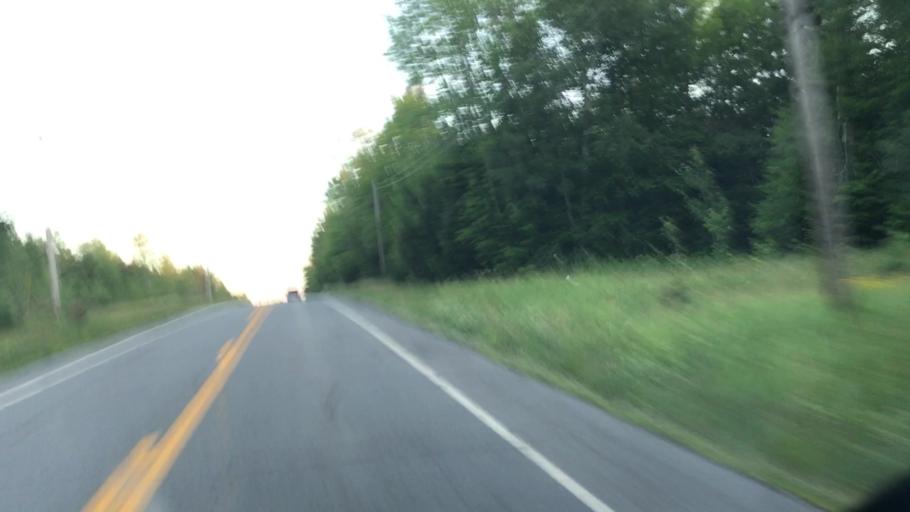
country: US
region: Maine
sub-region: Penobscot County
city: Medway
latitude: 45.5955
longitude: -68.3113
